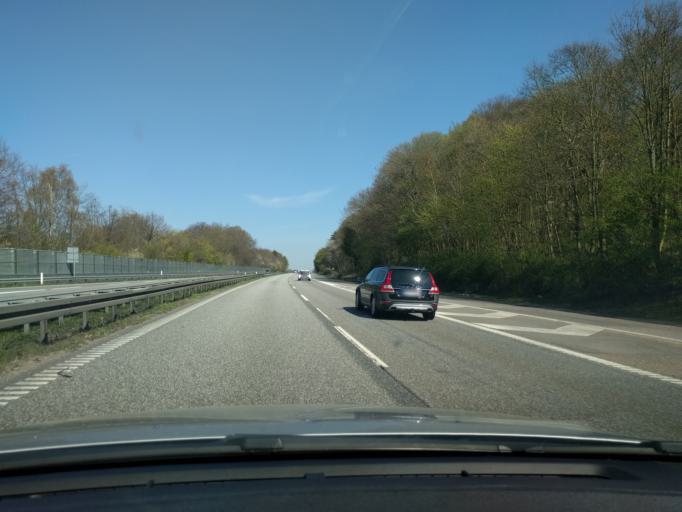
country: DK
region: Zealand
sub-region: Slagelse Kommune
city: Slagelse
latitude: 55.3981
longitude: 11.3829
